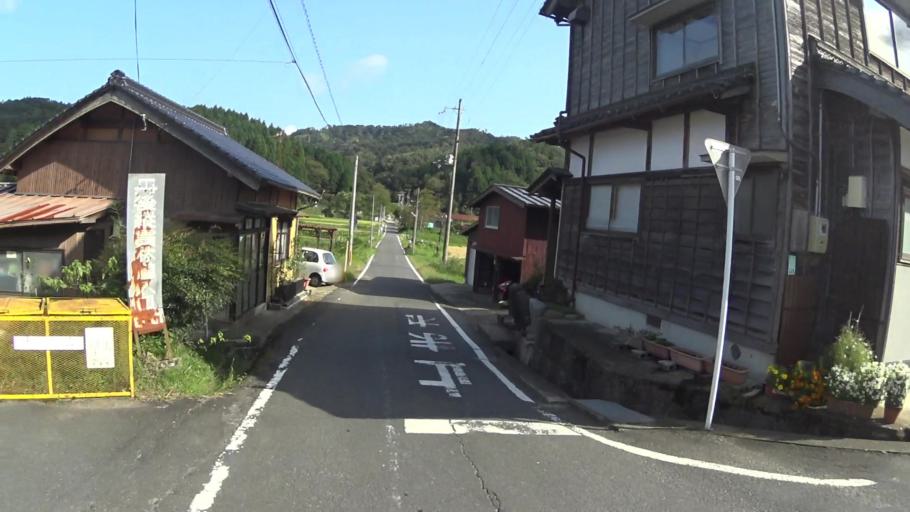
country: JP
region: Kyoto
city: Miyazu
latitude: 35.5693
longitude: 135.1160
